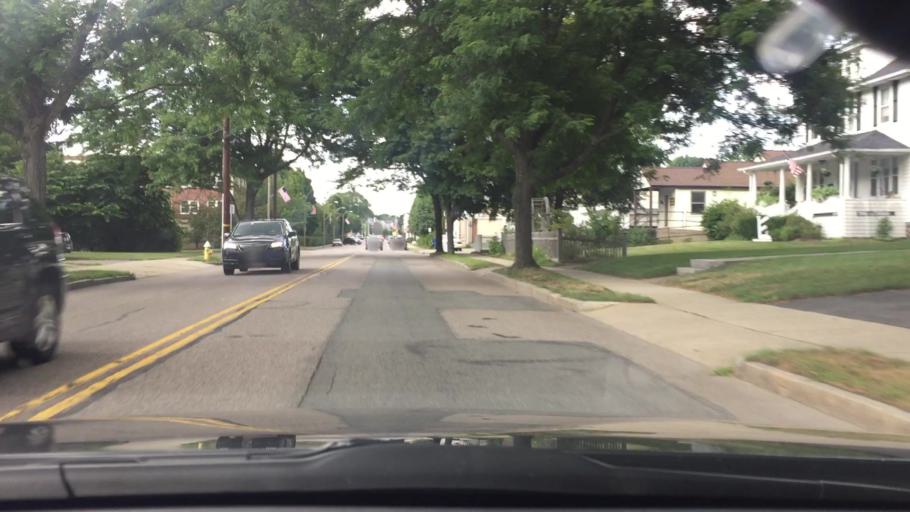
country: US
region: Massachusetts
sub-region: Norfolk County
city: Needham
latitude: 42.2903
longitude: -71.2350
